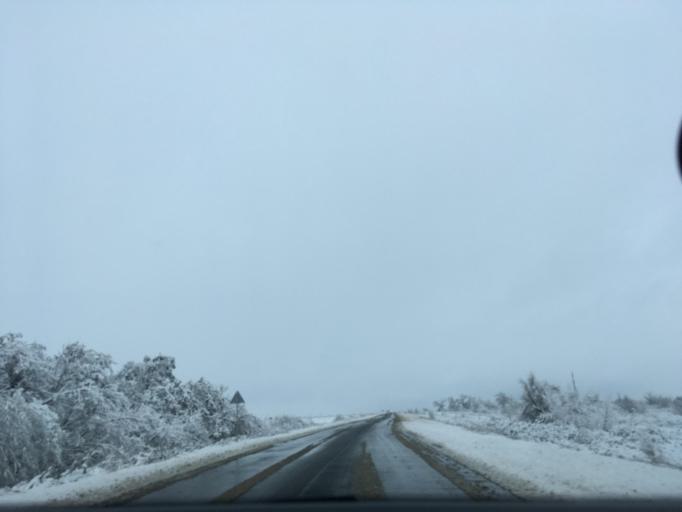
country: RU
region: Voronezj
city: Ol'khovatka
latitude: 50.1262
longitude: 39.1810
